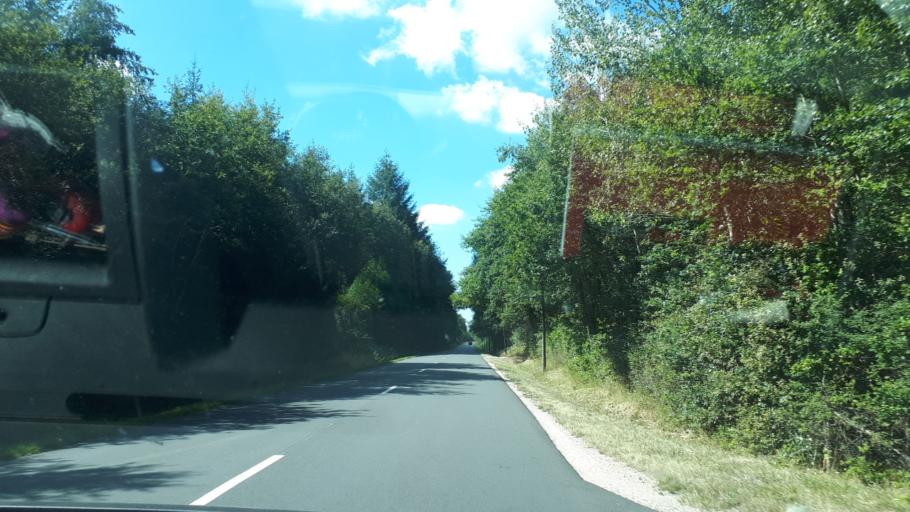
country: FR
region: Centre
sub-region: Departement du Loir-et-Cher
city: Chaumont-sur-Tharonne
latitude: 47.5720
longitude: 1.9193
